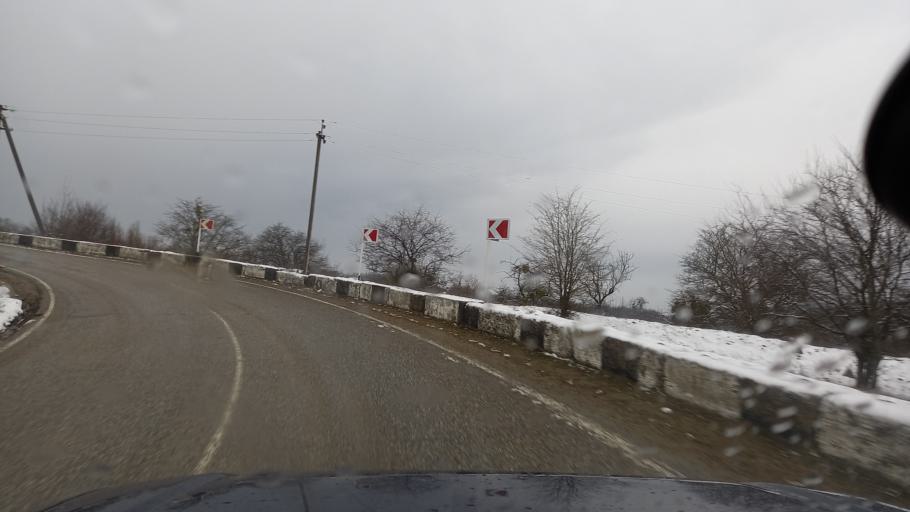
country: RU
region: Adygeya
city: Abadzekhskaya
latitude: 44.3558
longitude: 40.3085
